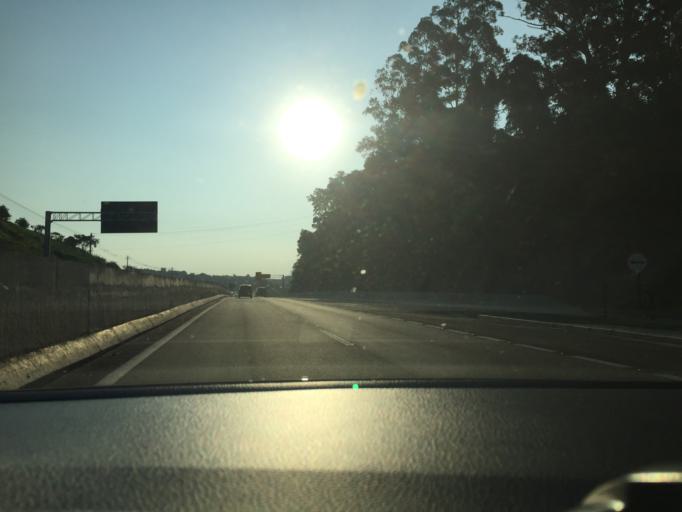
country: BR
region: Sao Paulo
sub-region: Louveira
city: Louveira
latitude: -23.0938
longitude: -46.9632
